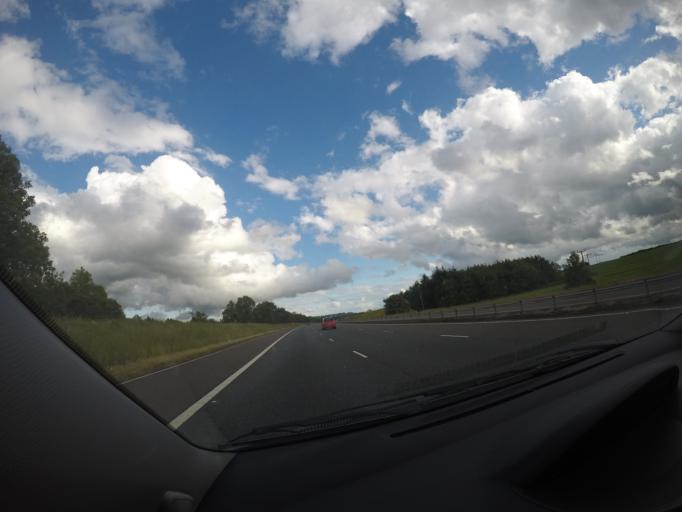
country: GB
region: Scotland
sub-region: Dumfries and Galloway
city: Lochmaben
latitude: 55.1729
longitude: -3.3960
